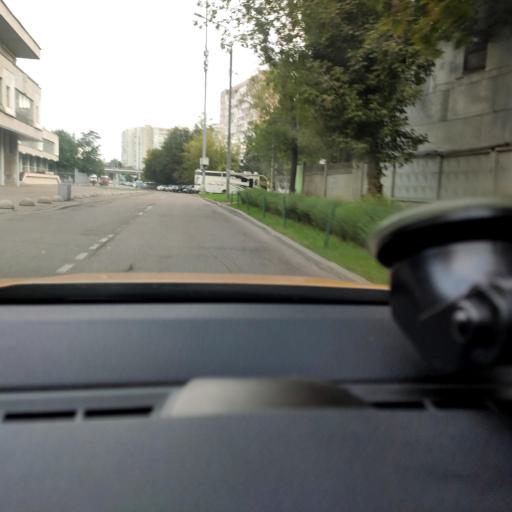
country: RU
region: Moscow
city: Vatutino
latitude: 55.8585
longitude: 37.6957
